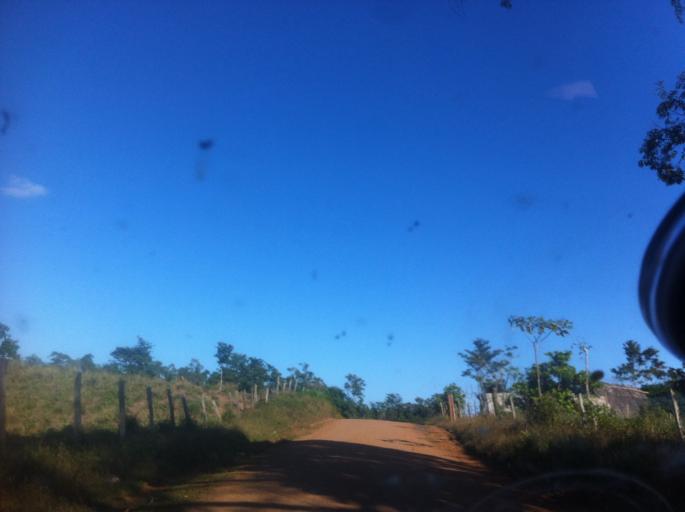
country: CR
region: Alajuela
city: Los Chiles
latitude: 11.0503
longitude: -84.4781
